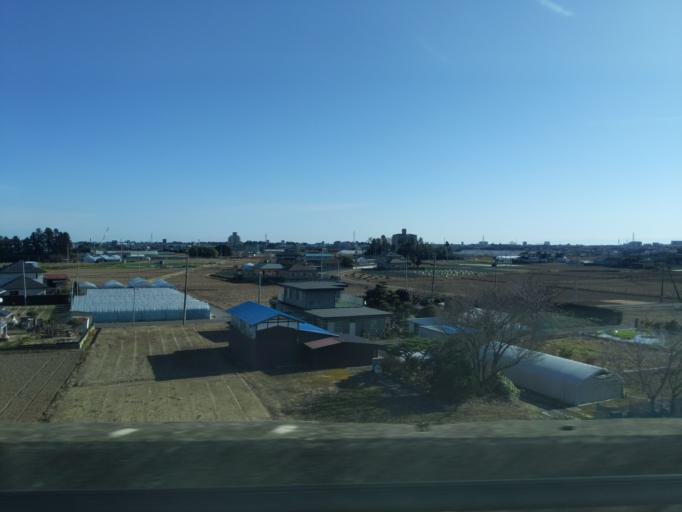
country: JP
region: Miyagi
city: Sendai
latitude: 38.1867
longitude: 140.8768
